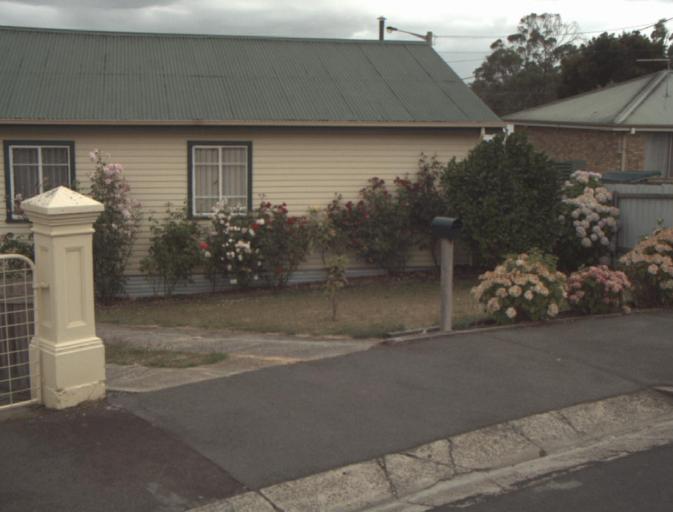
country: AU
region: Tasmania
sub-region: Launceston
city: Newstead
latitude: -41.4352
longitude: 147.1856
